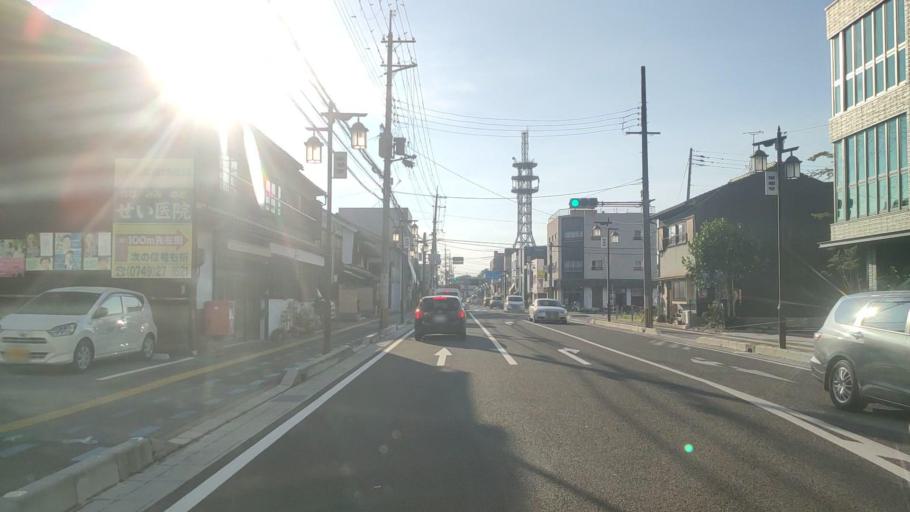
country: JP
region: Shiga Prefecture
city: Hikone
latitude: 35.2691
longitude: 136.2597
